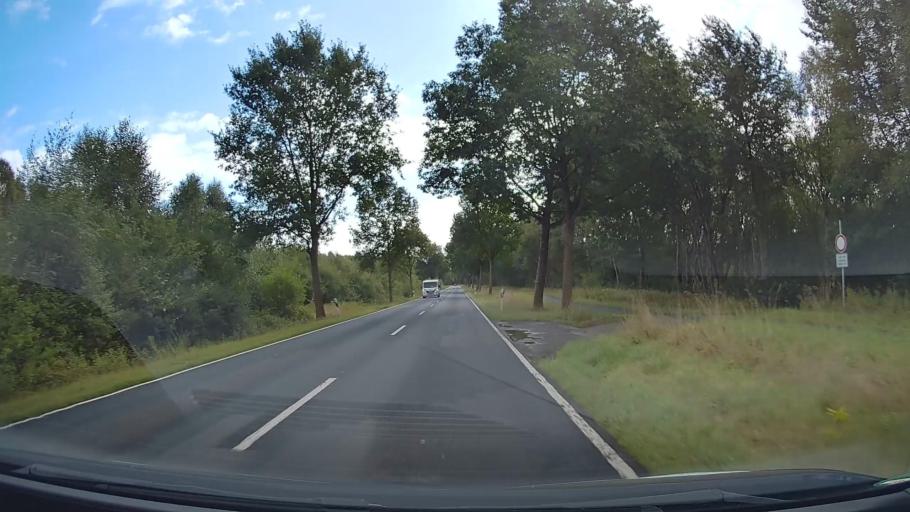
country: DE
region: Lower Saxony
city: Rhade
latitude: 53.3427
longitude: 9.0874
